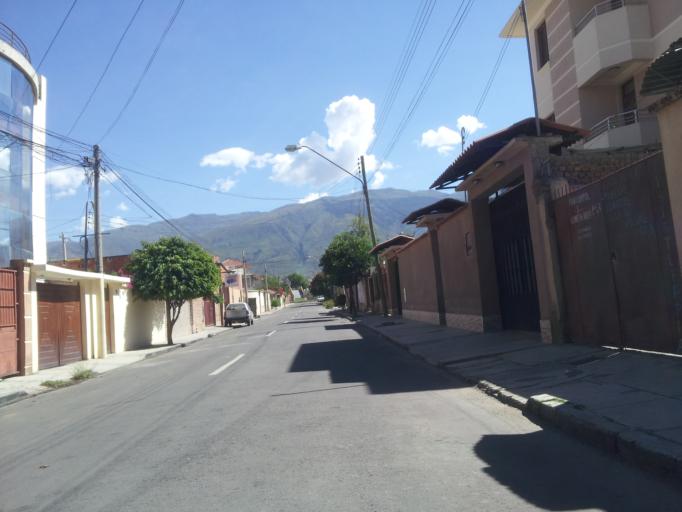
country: BO
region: Cochabamba
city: Cochabamba
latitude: -17.3758
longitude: -66.1750
